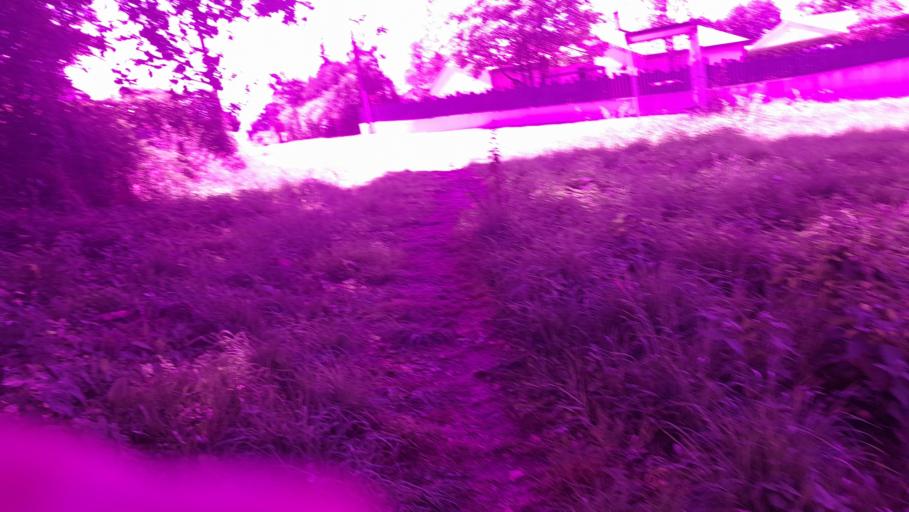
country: FR
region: Pays de la Loire
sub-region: Departement de la Loire-Atlantique
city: Oudon
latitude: 47.3518
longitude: -1.2850
